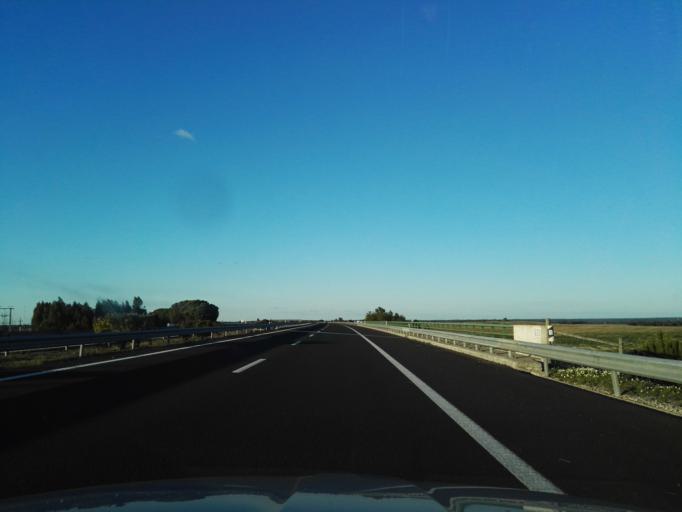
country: PT
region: Santarem
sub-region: Benavente
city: Poceirao
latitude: 38.7660
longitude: -8.6829
